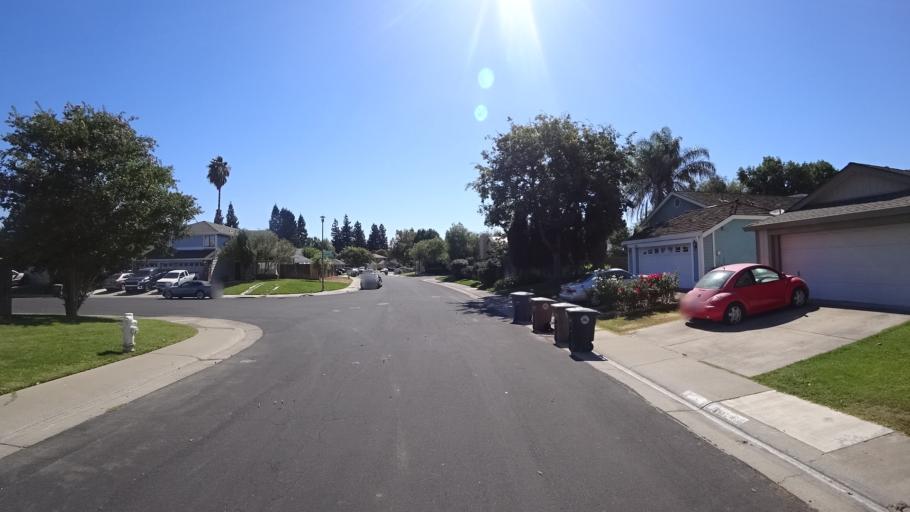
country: US
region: California
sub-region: Sacramento County
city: Laguna
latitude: 38.4262
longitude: -121.4325
